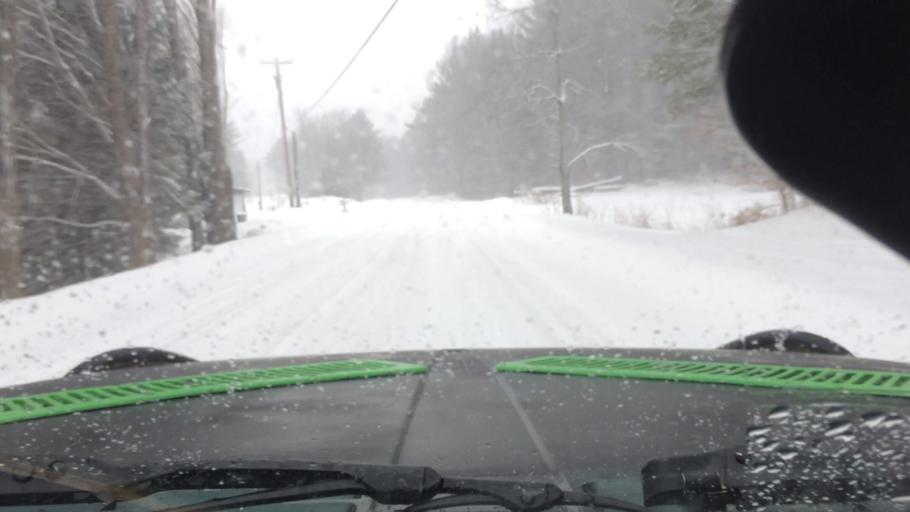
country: US
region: New York
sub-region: Oswego County
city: Constantia
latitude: 43.3054
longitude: -75.9211
